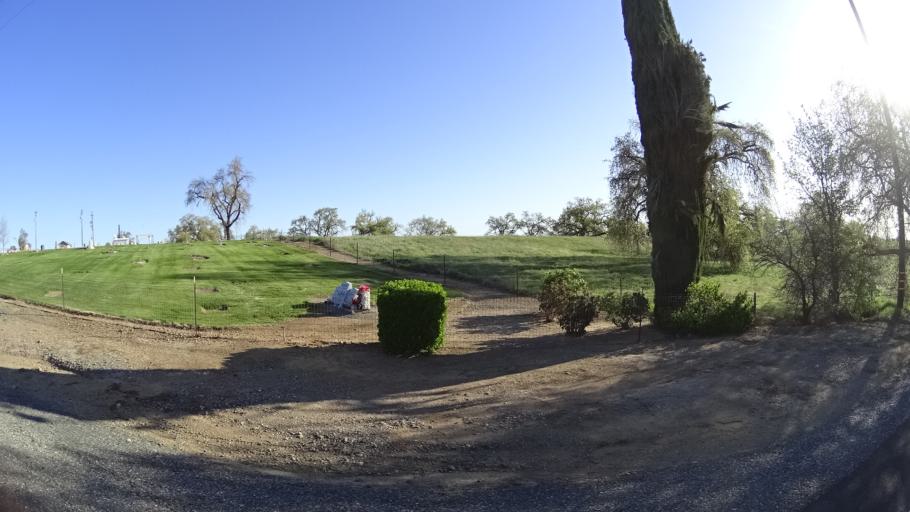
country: US
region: California
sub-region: Glenn County
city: Orland
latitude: 39.7819
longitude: -122.2943
